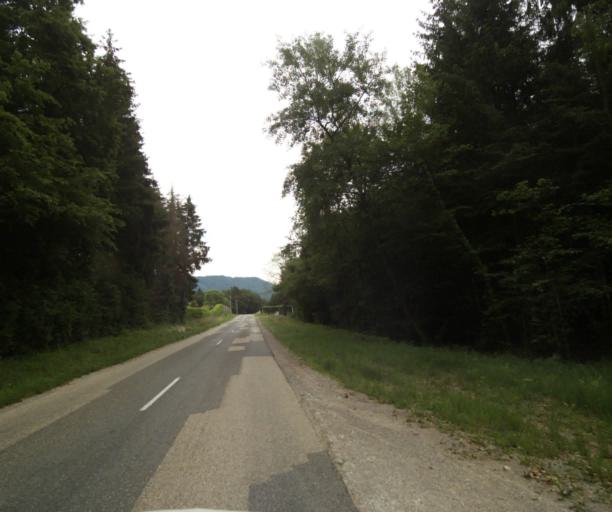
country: FR
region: Rhone-Alpes
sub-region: Departement de la Haute-Savoie
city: Perrignier
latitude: 46.3063
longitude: 6.4103
